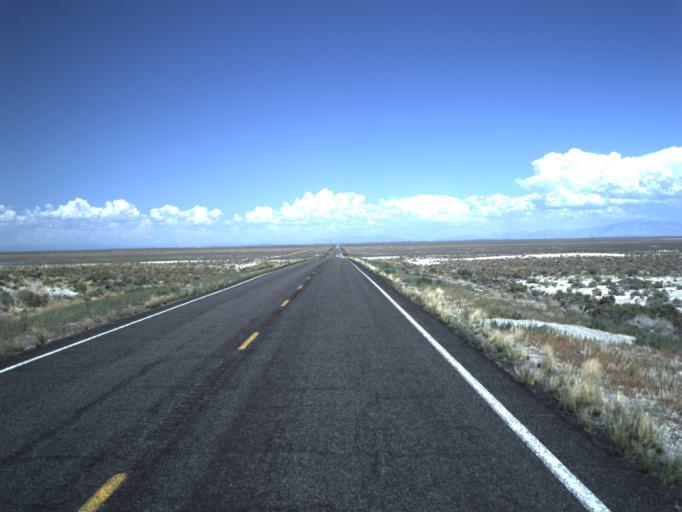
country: US
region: Utah
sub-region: Millard County
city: Delta
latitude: 39.1919
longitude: -112.9978
